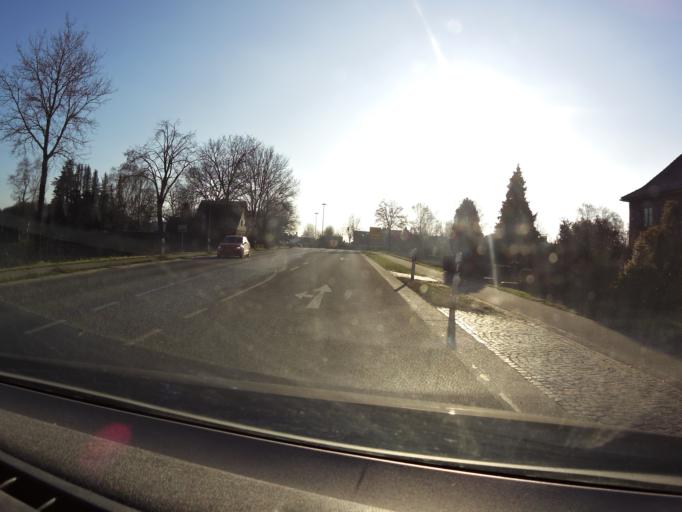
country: DE
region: North Rhine-Westphalia
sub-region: Regierungsbezirk Dusseldorf
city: Bruggen
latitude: 51.2537
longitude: 6.1835
